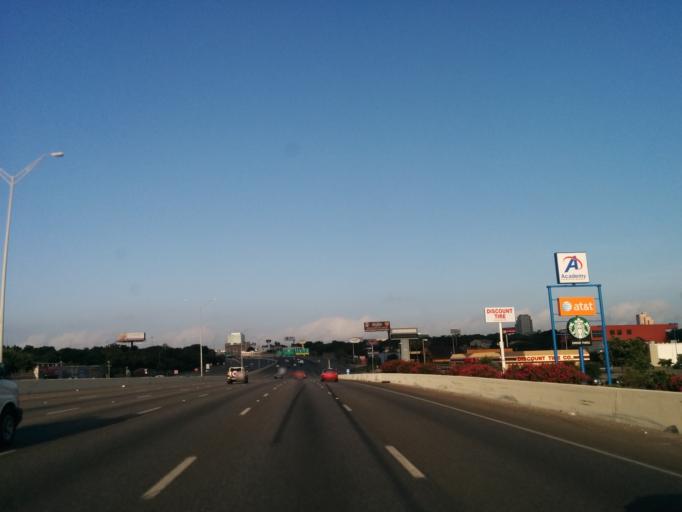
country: US
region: Texas
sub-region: Bexar County
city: Castle Hills
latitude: 29.5115
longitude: -98.5359
